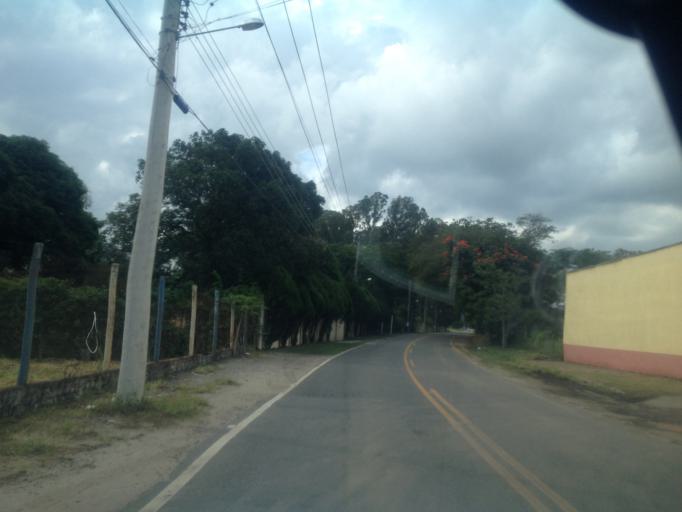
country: BR
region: Rio de Janeiro
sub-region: Quatis
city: Quatis
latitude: -22.4105
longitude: -44.2720
